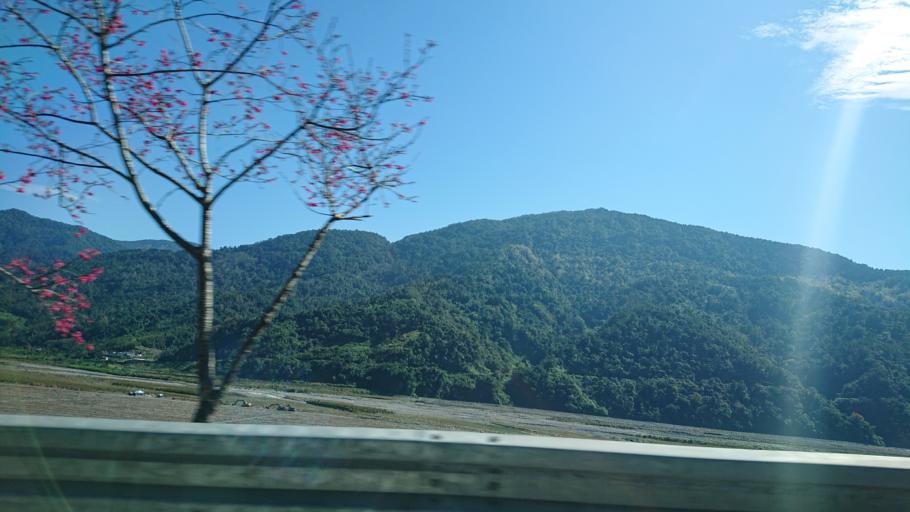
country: TW
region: Taiwan
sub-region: Yilan
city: Yilan
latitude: 24.5915
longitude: 121.5071
